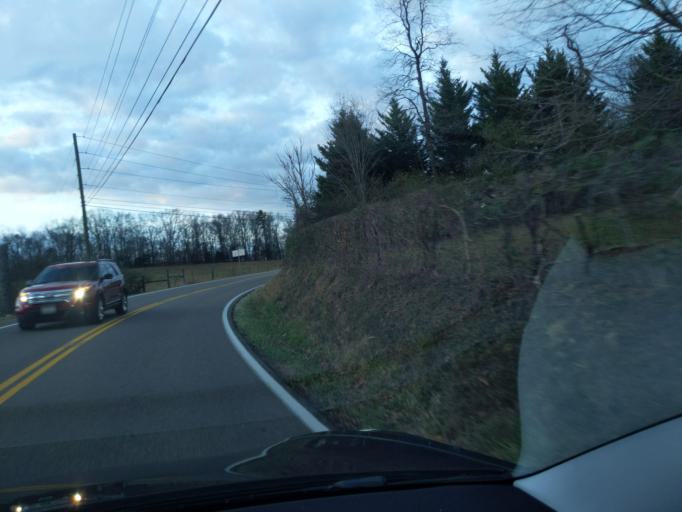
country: US
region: Tennessee
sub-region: Jefferson County
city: Dandridge
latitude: 36.0288
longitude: -83.4111
